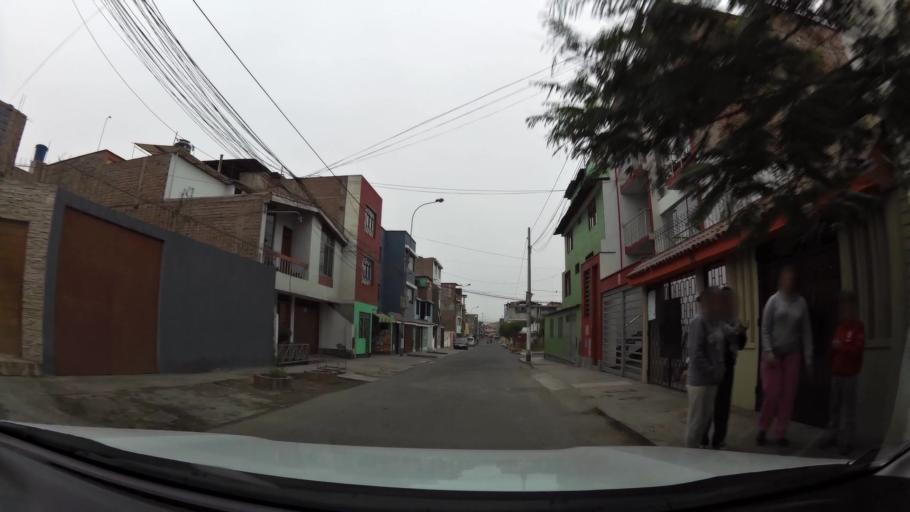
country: PE
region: Lima
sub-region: Lima
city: Surco
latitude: -12.1679
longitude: -76.9743
